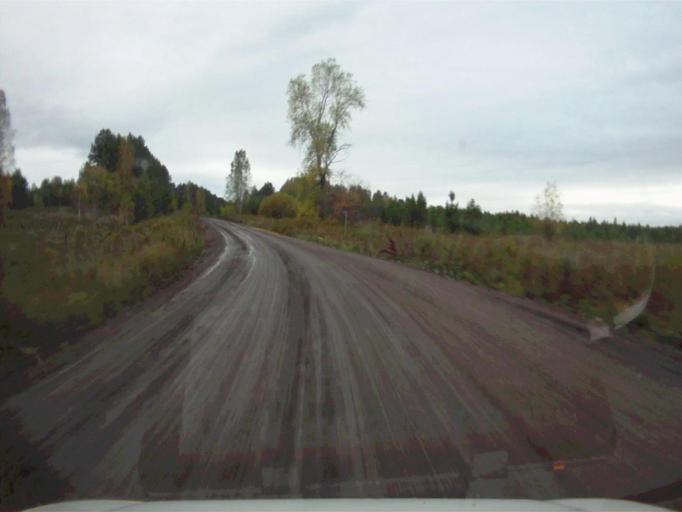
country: RU
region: Chelyabinsk
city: Nyazepetrovsk
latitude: 56.1396
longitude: 59.2972
